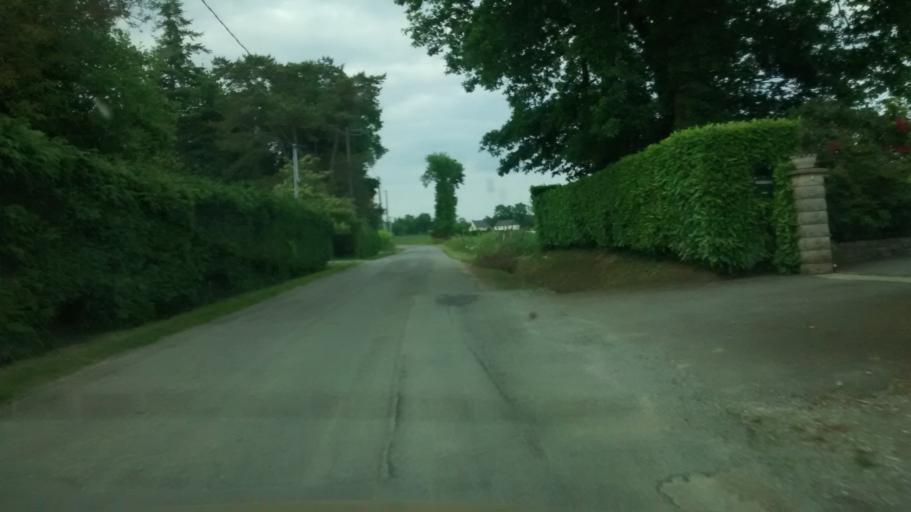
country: FR
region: Brittany
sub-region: Departement du Morbihan
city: Molac
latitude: 47.7256
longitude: -2.4268
